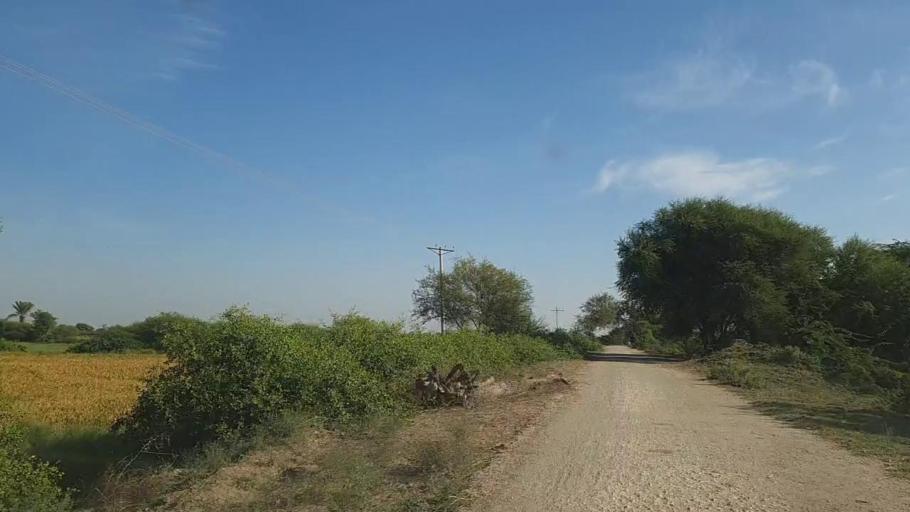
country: PK
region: Sindh
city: Bulri
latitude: 24.7840
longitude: 68.3513
